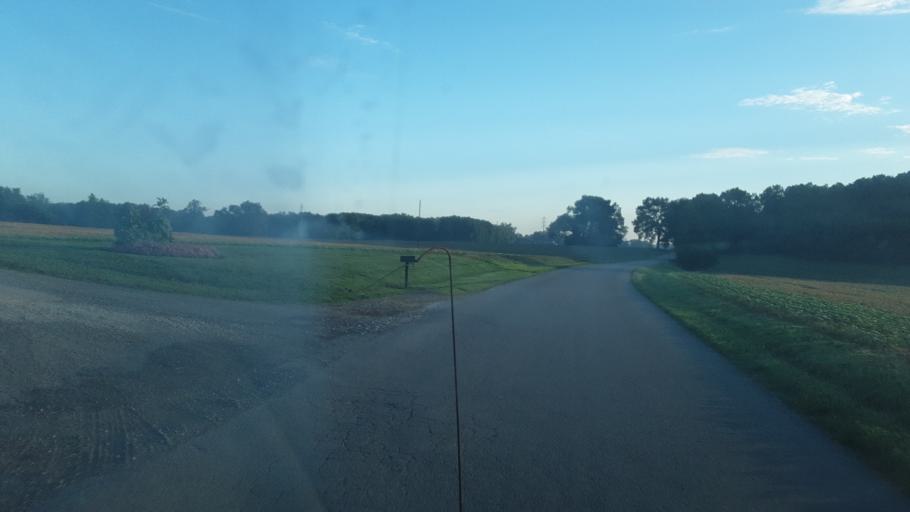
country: US
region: Kentucky
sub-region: Todd County
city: Guthrie
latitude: 36.7127
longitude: -87.1715
